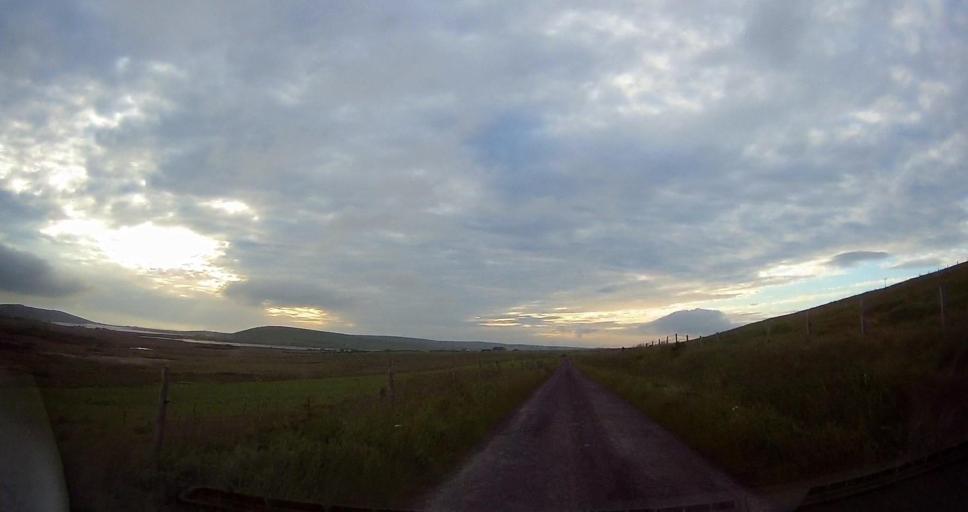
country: GB
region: Scotland
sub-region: Orkney Islands
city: Stromness
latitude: 59.1036
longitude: -3.2121
